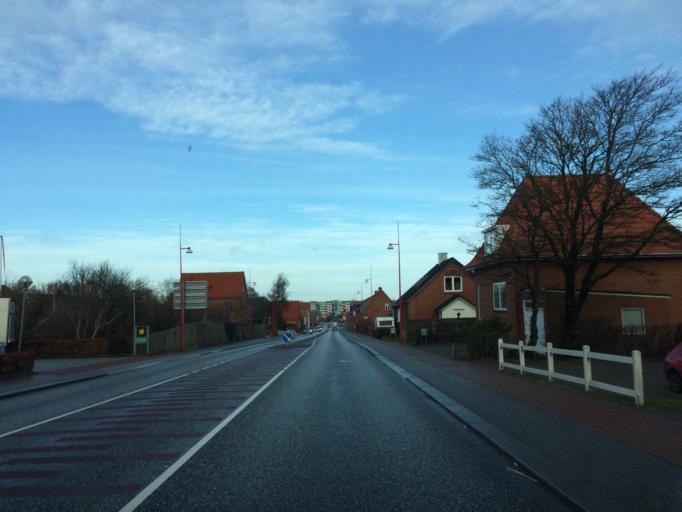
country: DK
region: Central Jutland
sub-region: Struer Kommune
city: Struer
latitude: 56.4886
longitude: 8.5837
